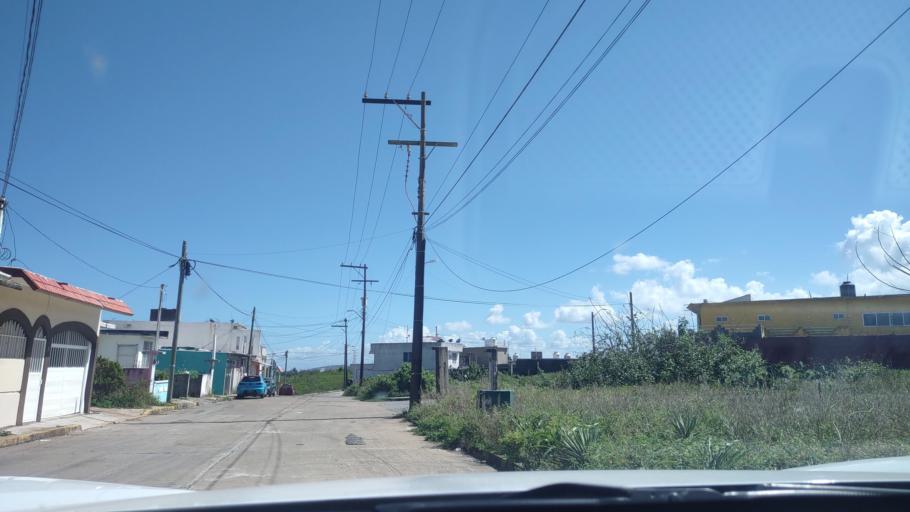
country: MX
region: Veracruz
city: Heroica Alvarado
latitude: 18.7829
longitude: -95.7736
